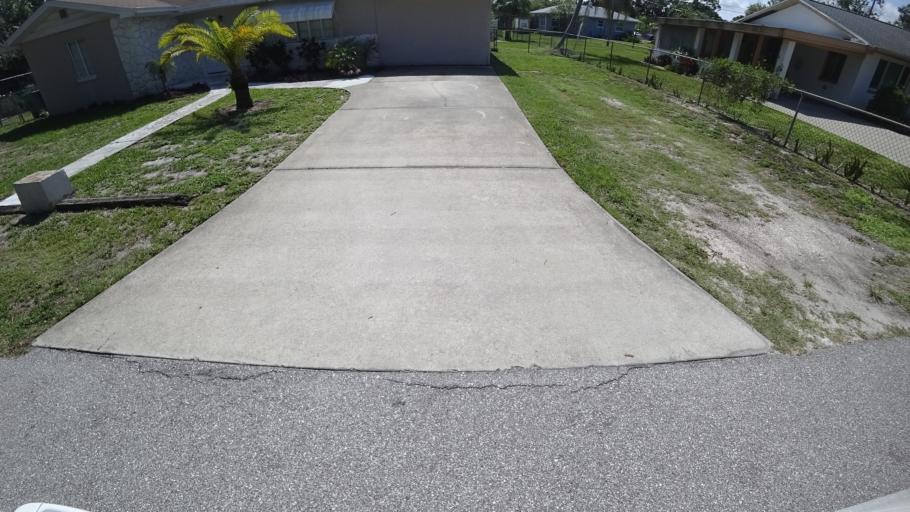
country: US
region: Florida
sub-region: Manatee County
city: Whitfield
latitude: 27.3898
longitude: -82.5623
